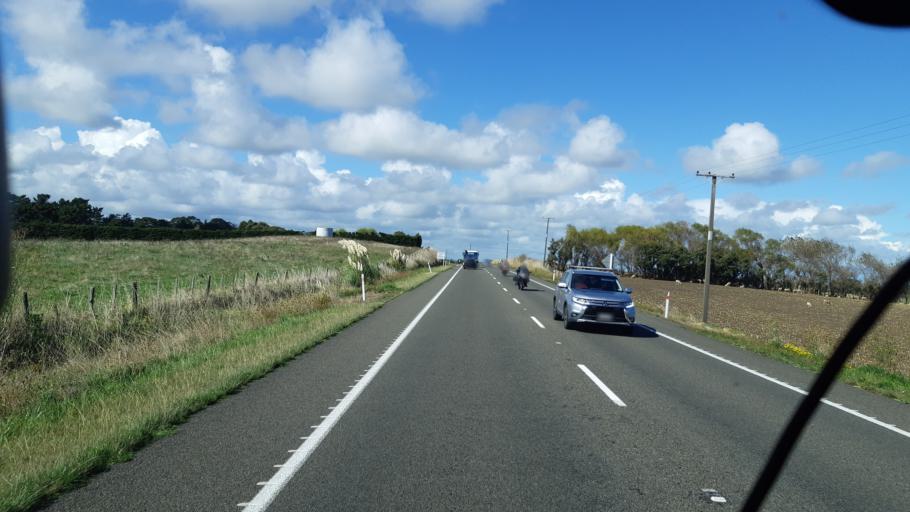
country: NZ
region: Manawatu-Wanganui
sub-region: Wanganui District
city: Wanganui
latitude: -39.9773
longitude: 175.1342
